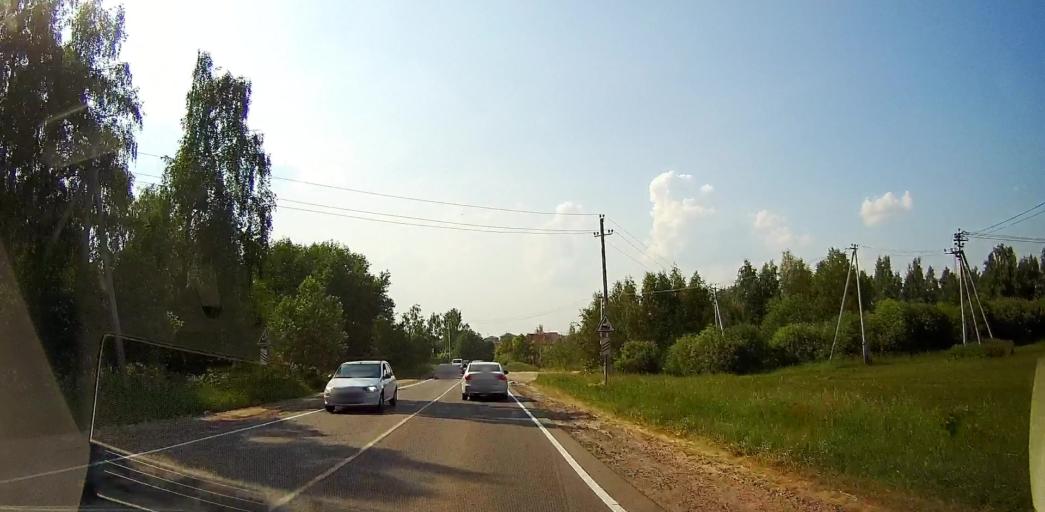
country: RU
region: Moskovskaya
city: Zhitnevo
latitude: 55.3101
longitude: 37.9043
